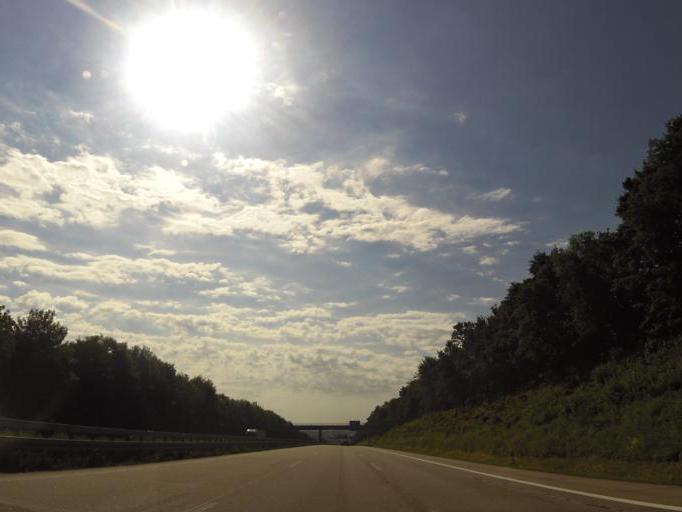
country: DE
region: Baden-Wuerttemberg
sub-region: Regierungsbezirk Stuttgart
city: Denkendorf
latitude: 48.6807
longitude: 9.3332
